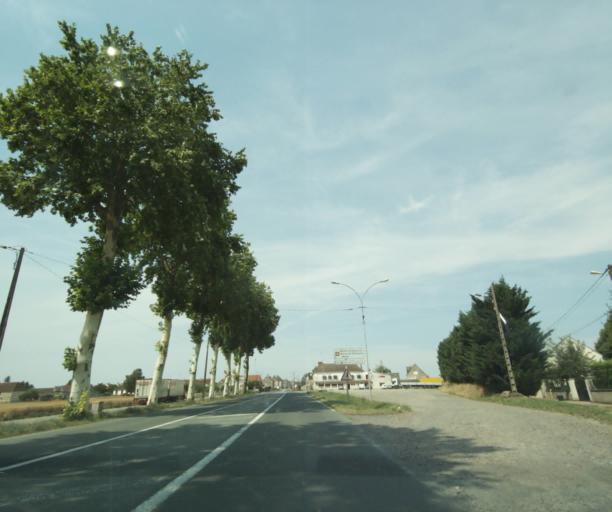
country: FR
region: Centre
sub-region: Departement d'Indre-et-Loire
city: La Celle-Saint-Avant
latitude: 47.0184
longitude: 0.6032
